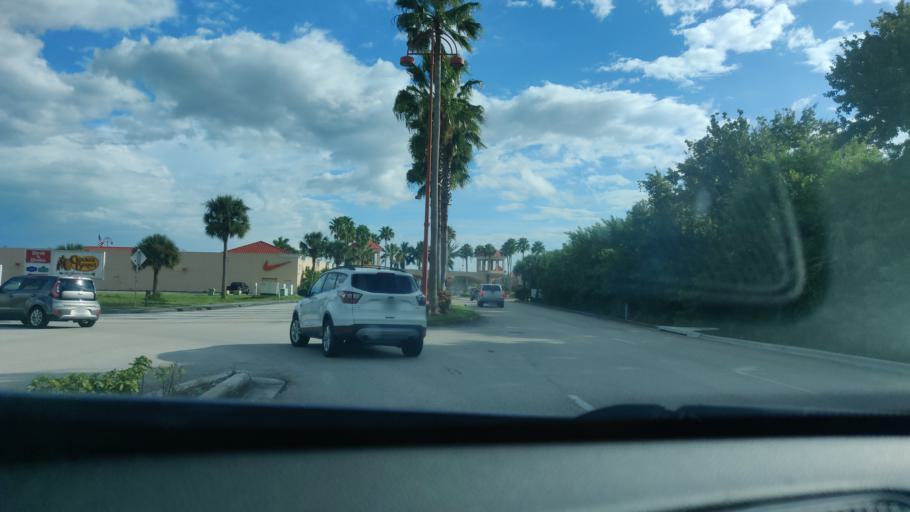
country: US
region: Florida
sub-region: Indian River County
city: West Vero Corridor
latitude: 27.6380
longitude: -80.5224
